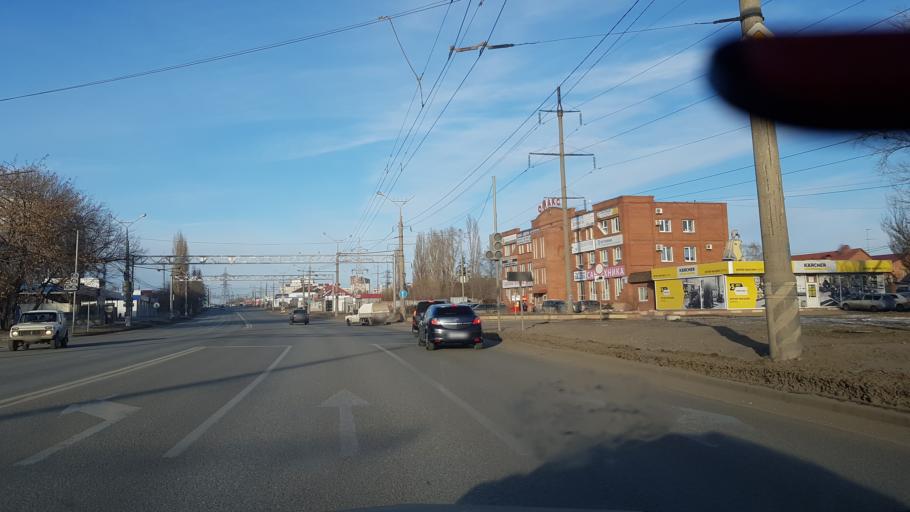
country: RU
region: Samara
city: Tol'yatti
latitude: 53.5310
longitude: 49.3966
